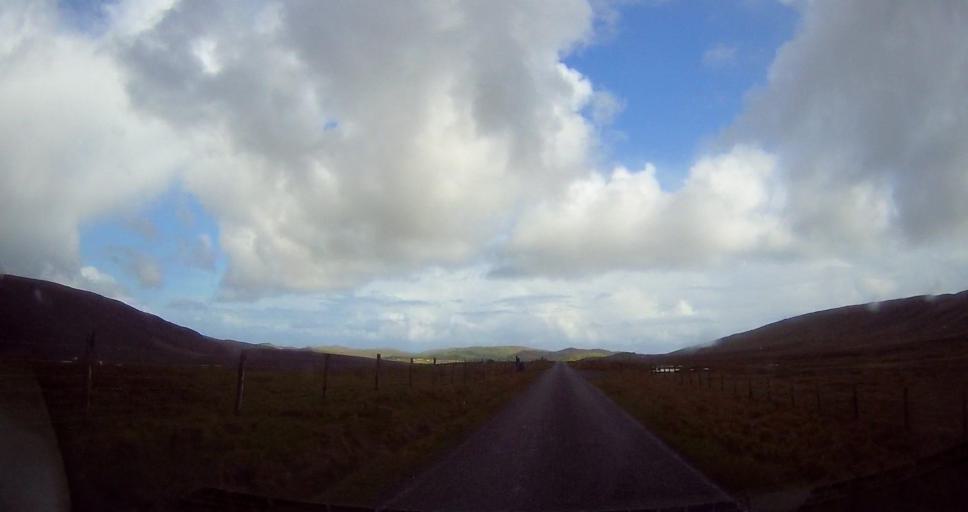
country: GB
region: Scotland
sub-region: Shetland Islands
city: Lerwick
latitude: 60.5599
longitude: -1.3364
